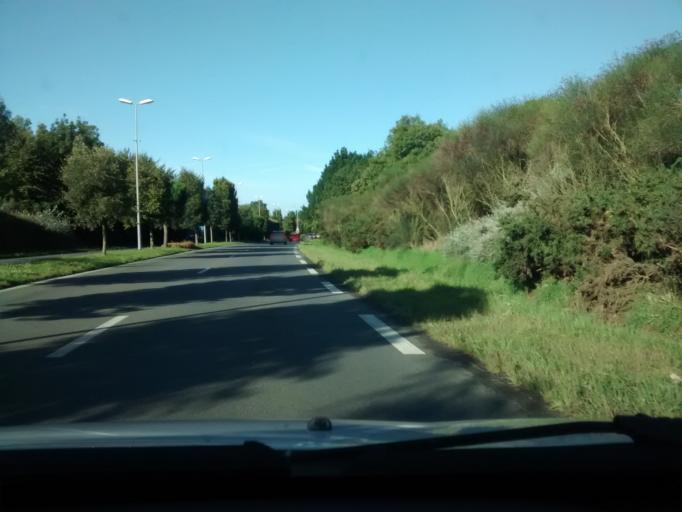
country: FR
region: Brittany
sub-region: Departement d'Ille-et-Vilaine
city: Saint-Malo
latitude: 48.6485
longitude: -1.9795
